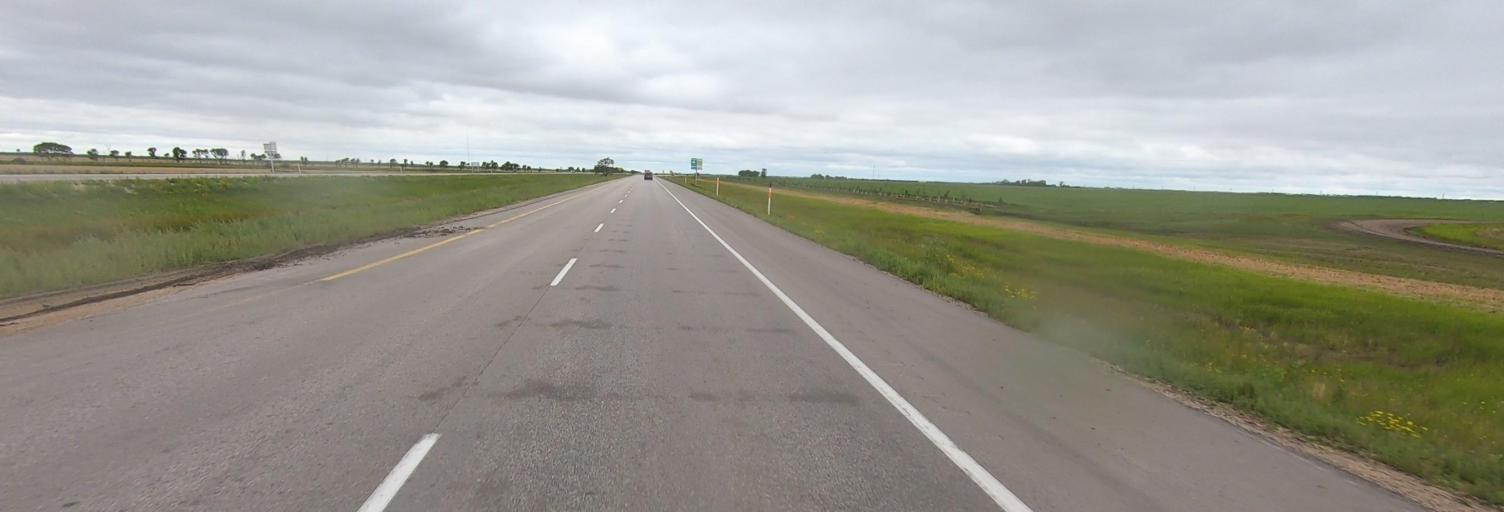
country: CA
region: Manitoba
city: Headingley
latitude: 49.8871
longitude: -97.6415
